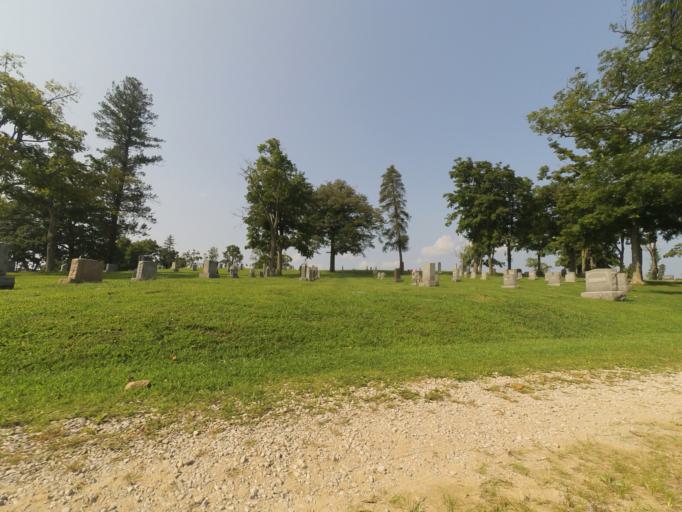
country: US
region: West Virginia
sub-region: Cabell County
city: Huntington
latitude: 38.4037
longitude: -82.3963
